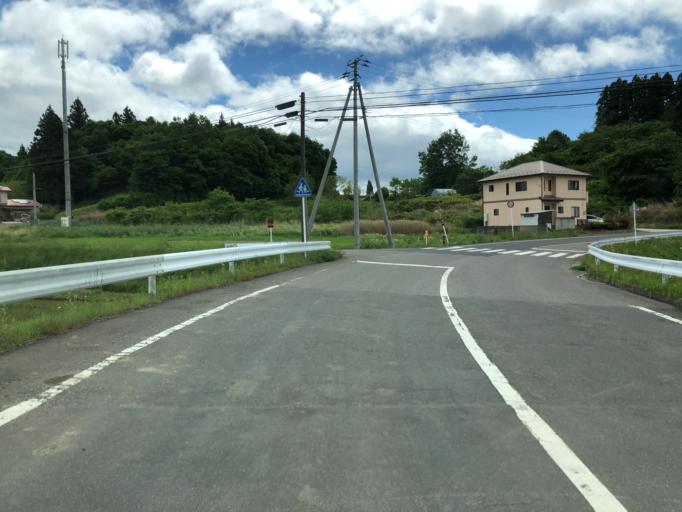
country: JP
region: Fukushima
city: Motomiya
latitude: 37.5166
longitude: 140.4739
